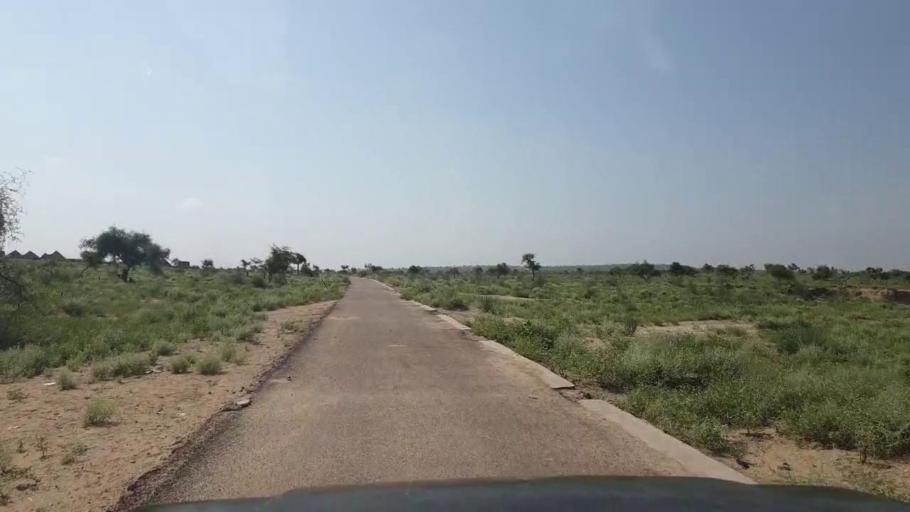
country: PK
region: Sindh
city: Islamkot
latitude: 25.1824
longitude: 70.3925
